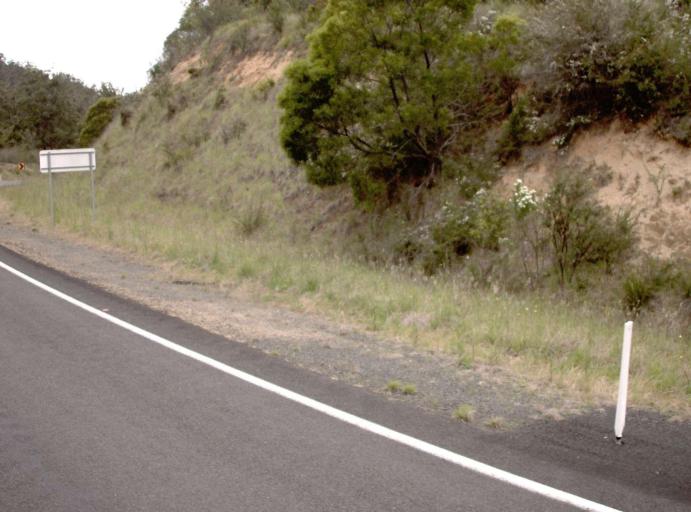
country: AU
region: New South Wales
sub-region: Bombala
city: Bombala
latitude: -37.2412
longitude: 149.2601
